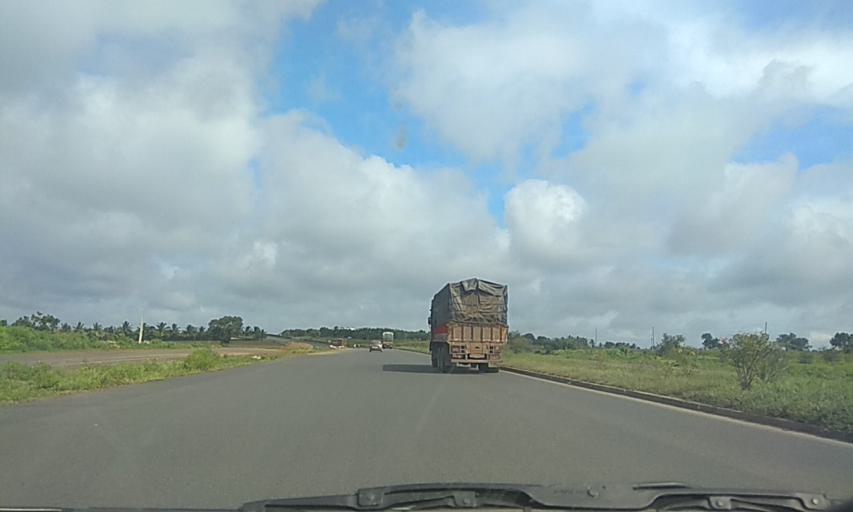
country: IN
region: Karnataka
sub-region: Haveri
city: Shiggaon
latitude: 15.0030
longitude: 75.2052
